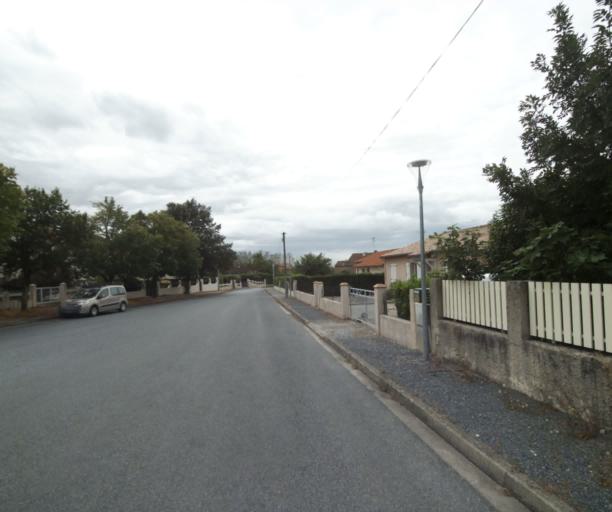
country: FR
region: Midi-Pyrenees
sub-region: Departement du Tarn
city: Soreze
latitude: 43.4567
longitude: 2.0574
